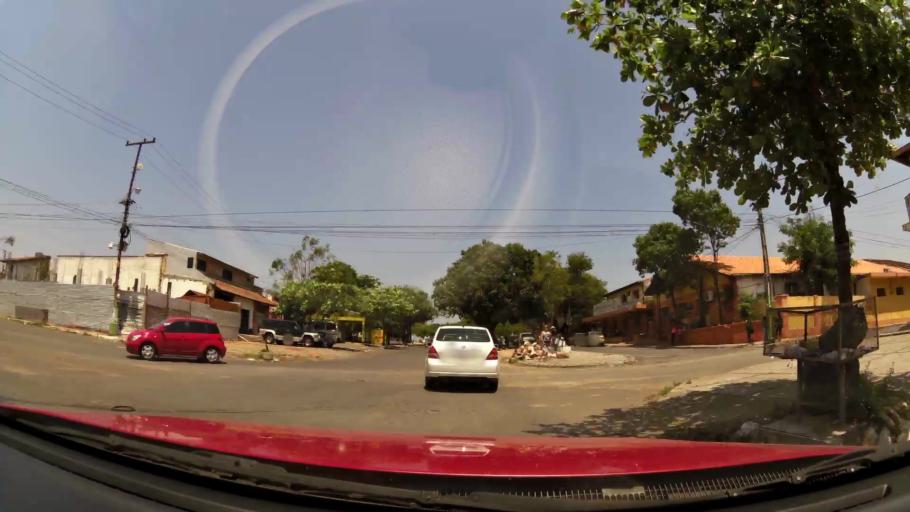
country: PY
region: Asuncion
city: Asuncion
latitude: -25.2991
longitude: -57.6438
